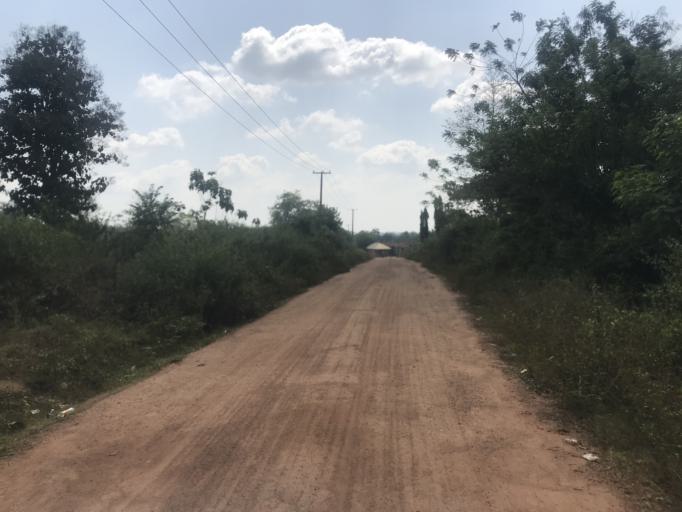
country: NG
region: Osun
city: Iragbiji
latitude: 7.8926
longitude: 4.7020
